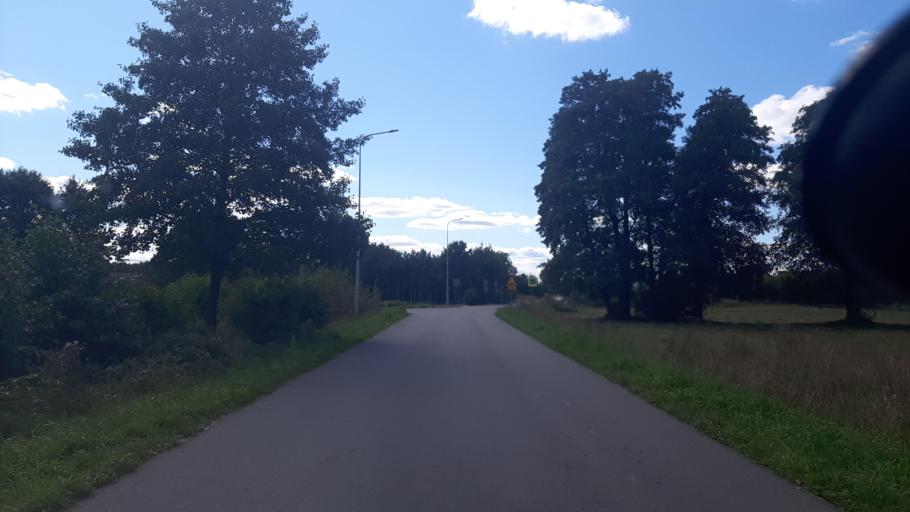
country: PL
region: Lublin Voivodeship
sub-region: Powiat lubelski
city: Garbow
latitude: 51.4037
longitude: 22.3568
